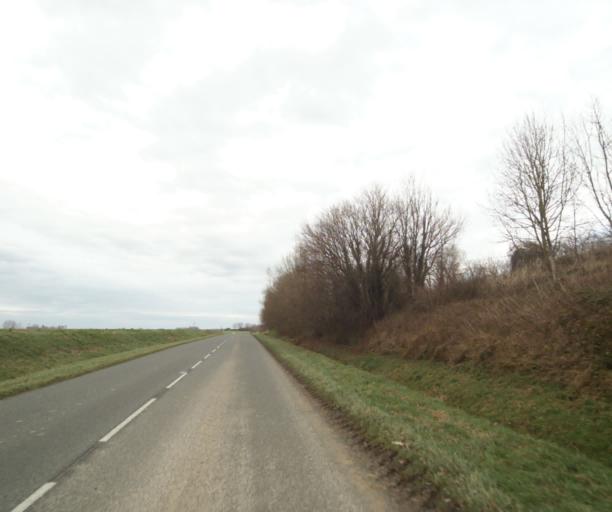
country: FR
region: Nord-Pas-de-Calais
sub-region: Departement du Nord
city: Jenlain
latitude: 50.3271
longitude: 3.6334
